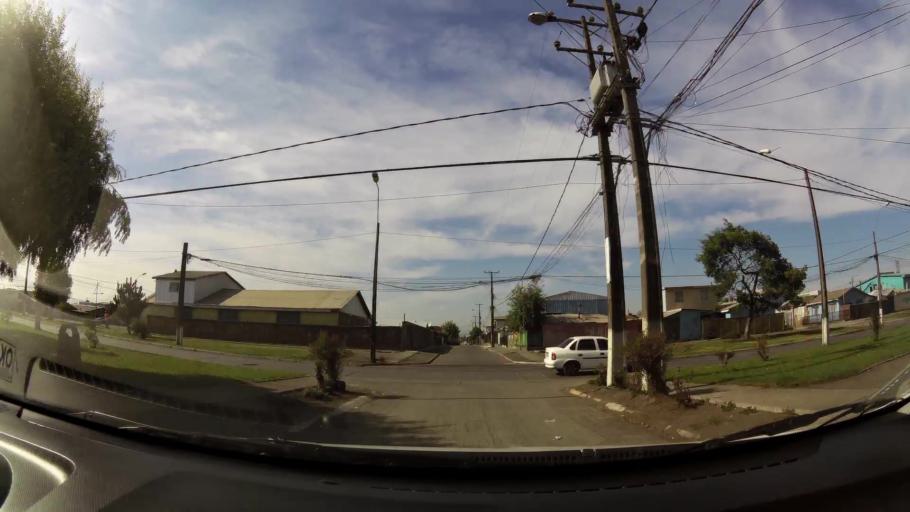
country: CL
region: Biobio
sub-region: Provincia de Concepcion
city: Talcahuano
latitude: -36.7794
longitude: -73.1130
